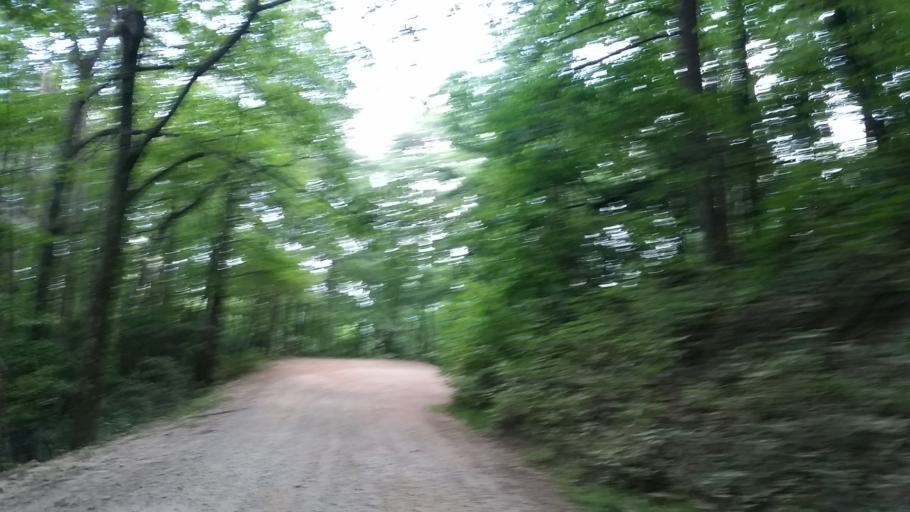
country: US
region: Georgia
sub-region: Lumpkin County
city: Dahlonega
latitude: 34.6383
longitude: -84.0985
